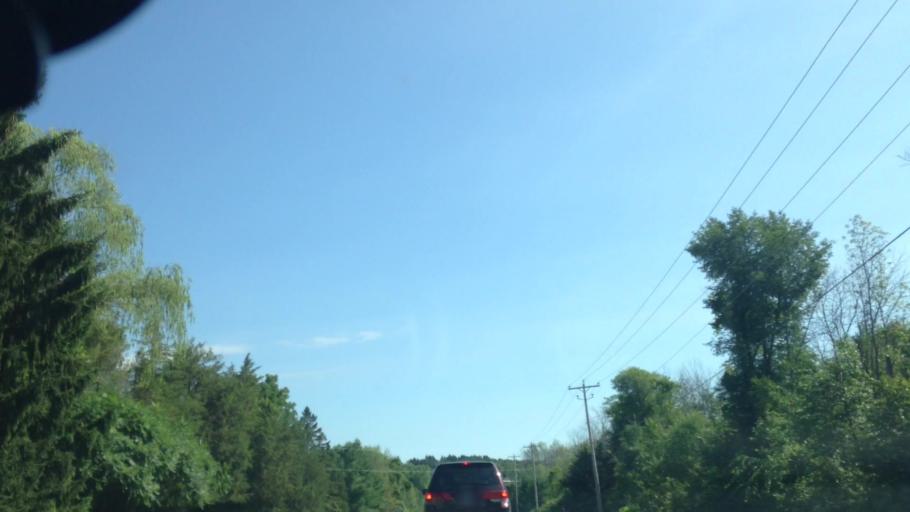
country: US
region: Wisconsin
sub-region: Washington County
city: Slinger
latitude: 43.3793
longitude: -88.2463
